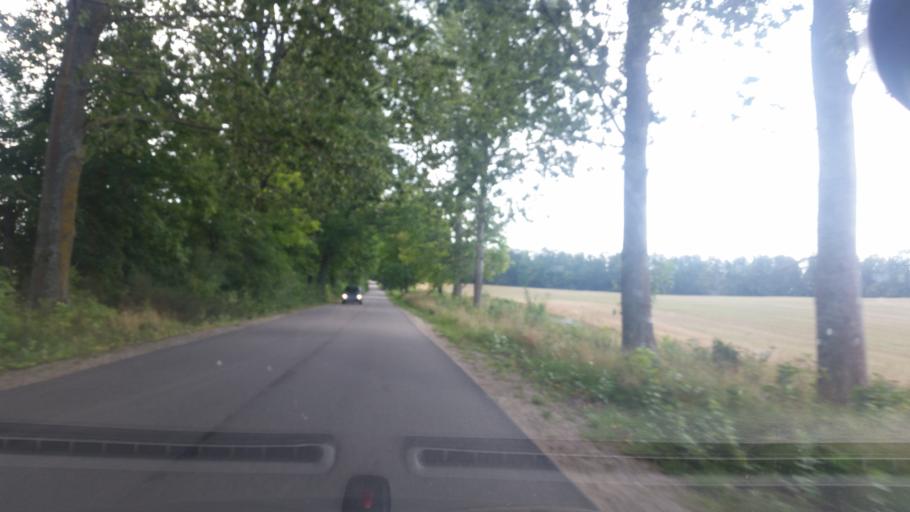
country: PL
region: Pomeranian Voivodeship
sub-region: Powiat wejherowski
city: Choczewo
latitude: 54.7524
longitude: 17.7927
